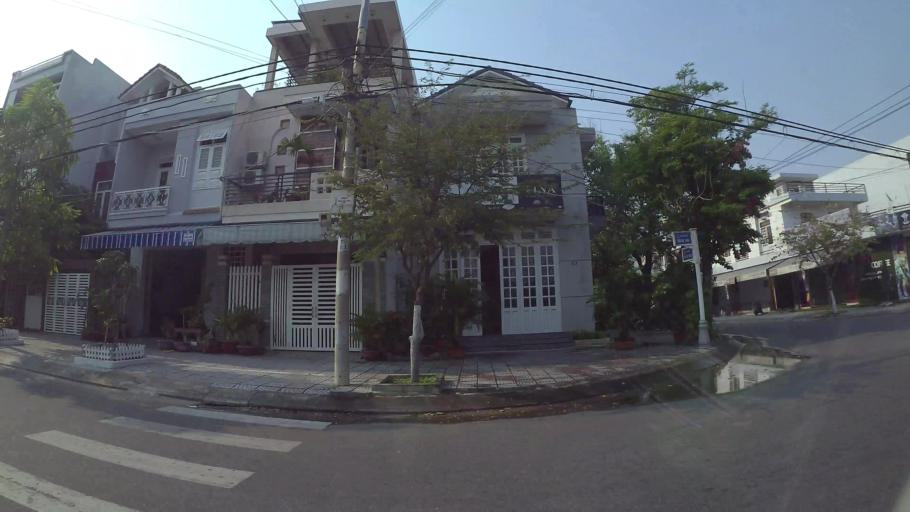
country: VN
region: Da Nang
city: Cam Le
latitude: 16.0212
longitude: 108.2092
